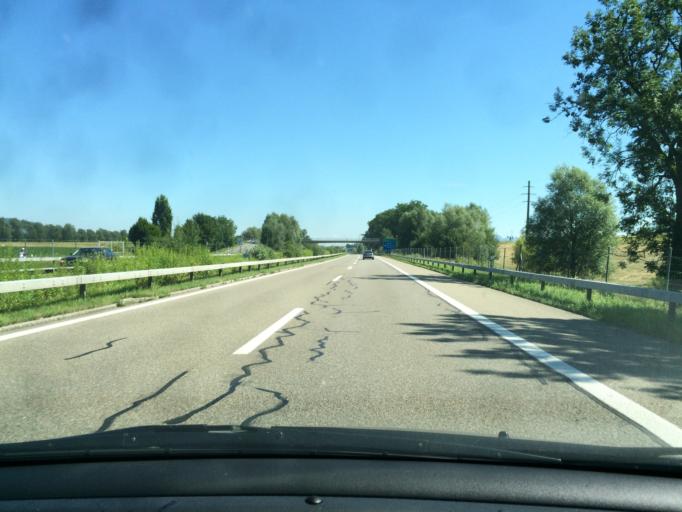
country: CH
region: Saint Gallen
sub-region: Wahlkreis Rheintal
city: Diepoldsau
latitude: 47.3816
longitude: 9.6376
